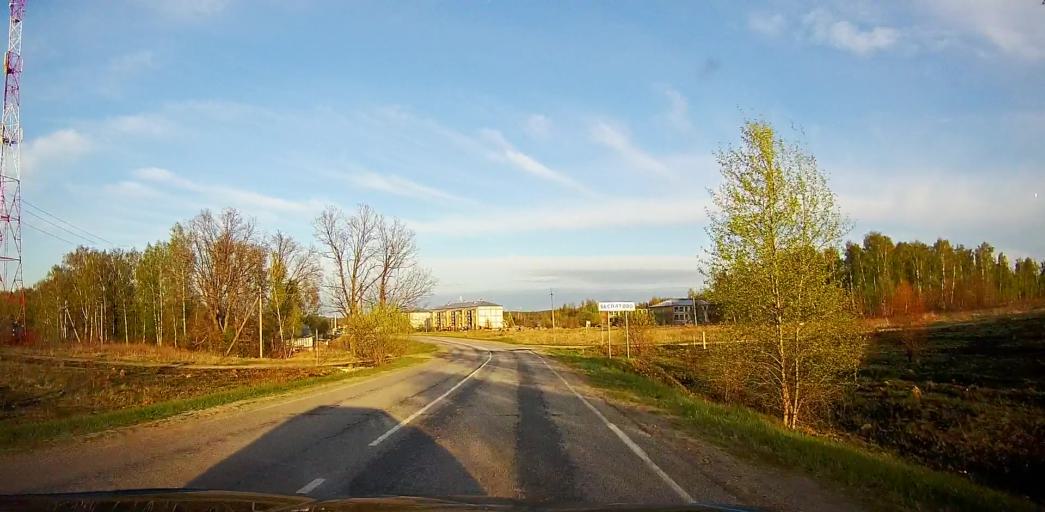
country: RU
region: Moskovskaya
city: Meshcherino
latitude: 55.2344
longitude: 38.3573
